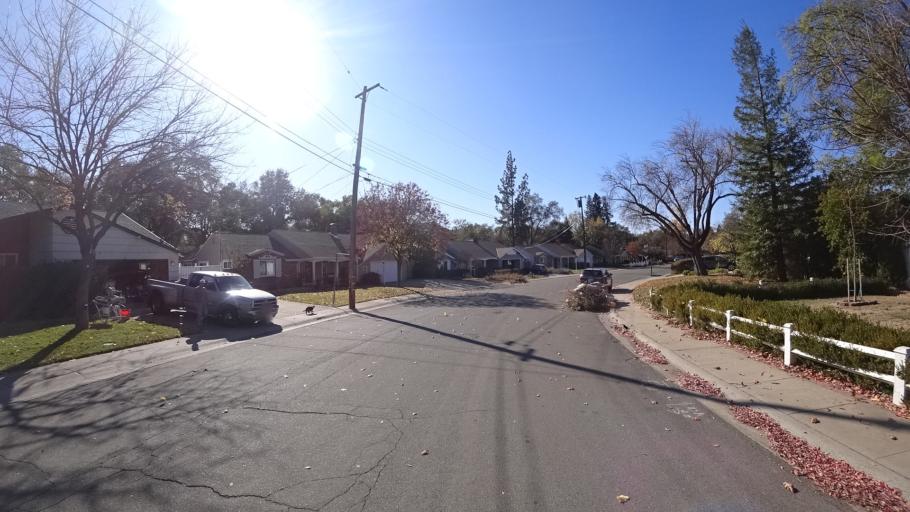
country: US
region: California
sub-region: Sacramento County
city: Foothill Farms
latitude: 38.6750
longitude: -121.3175
